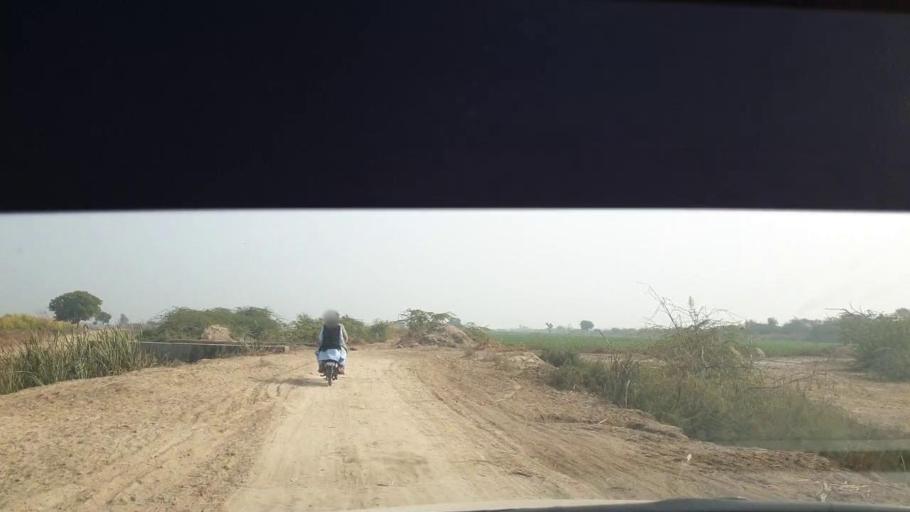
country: PK
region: Sindh
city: Berani
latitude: 25.8100
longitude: 68.8399
